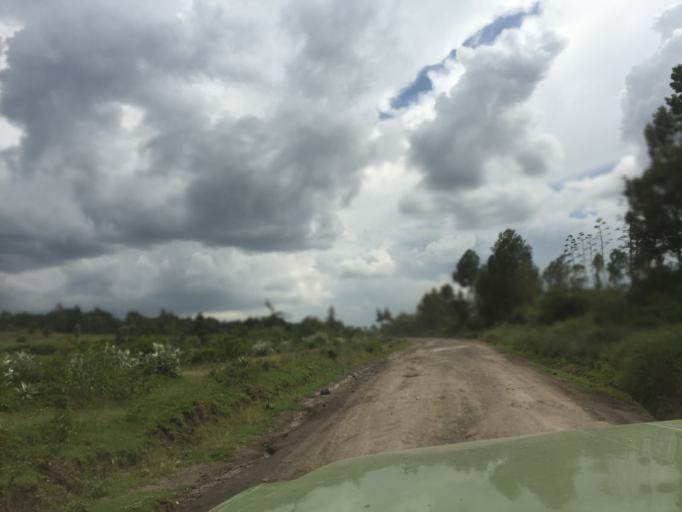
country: KE
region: Nyandarua
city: Ol Kalou
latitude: -0.4675
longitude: 36.4087
